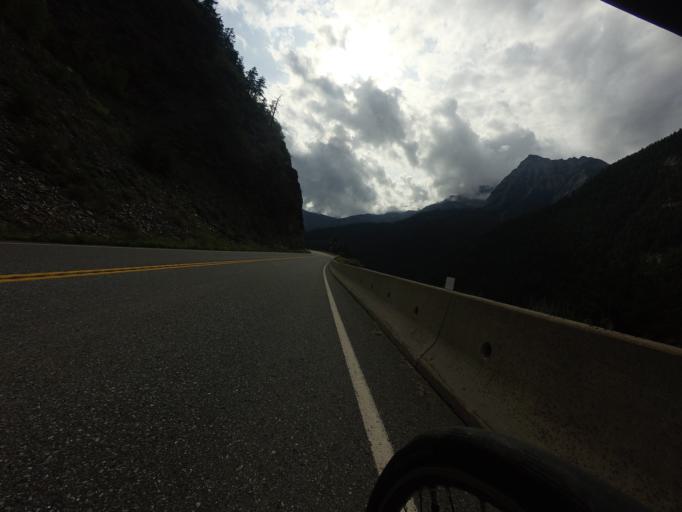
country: CA
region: British Columbia
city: Lillooet
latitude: 50.6418
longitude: -122.0428
